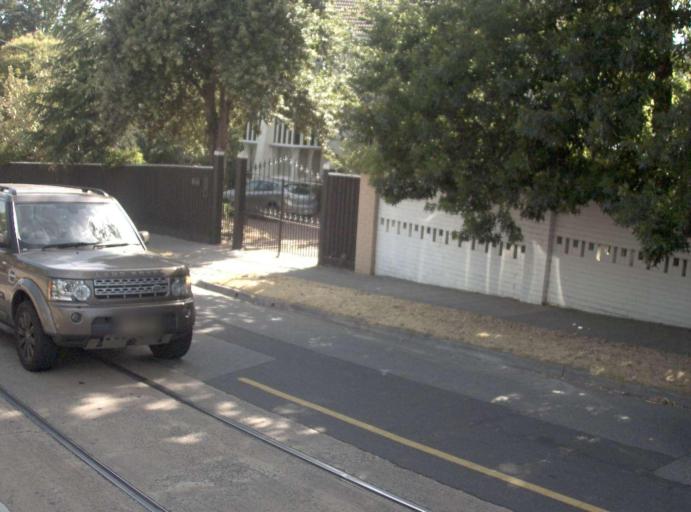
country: AU
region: Victoria
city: Toorak
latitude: -37.8431
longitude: 145.0316
